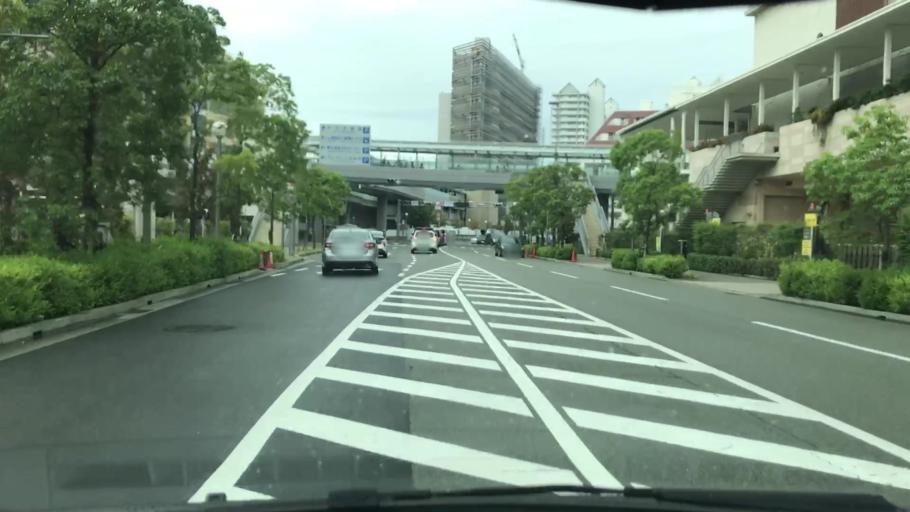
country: JP
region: Hyogo
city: Nishinomiya-hama
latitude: 34.7433
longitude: 135.3580
